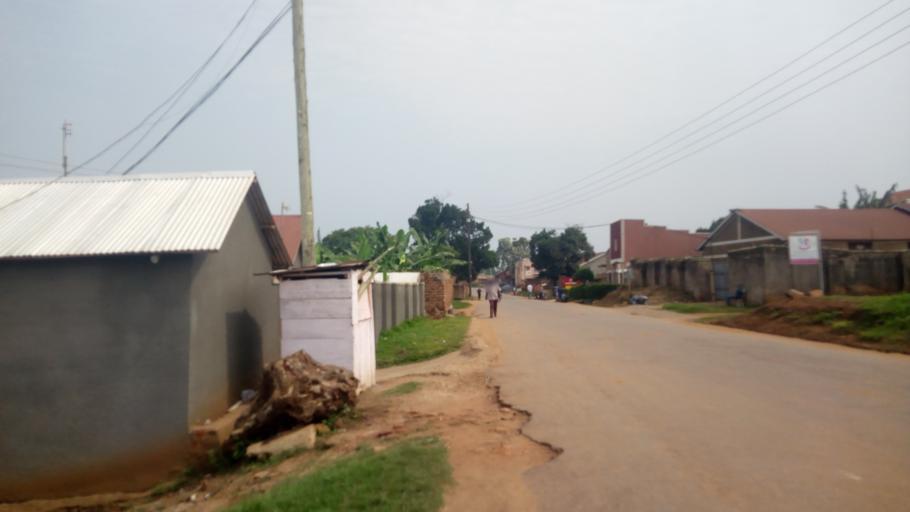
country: UG
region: Central Region
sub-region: Wakiso District
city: Kireka
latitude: 0.3046
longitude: 32.6510
